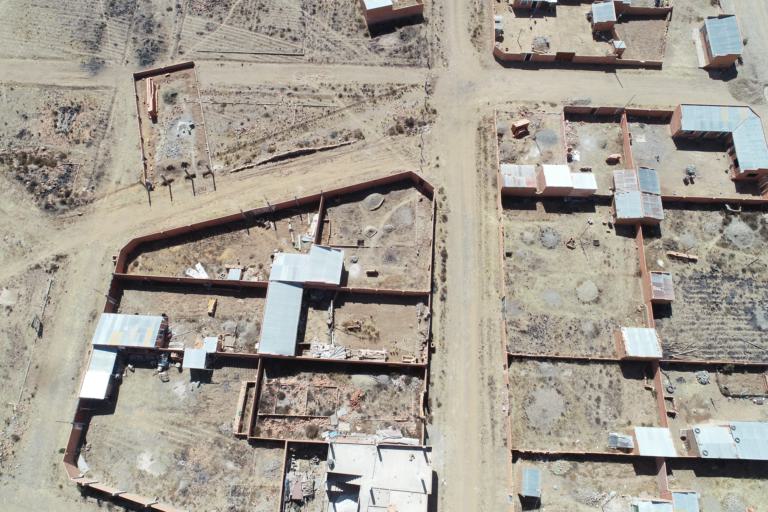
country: BO
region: La Paz
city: La Paz
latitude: -16.5964
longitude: -68.2119
